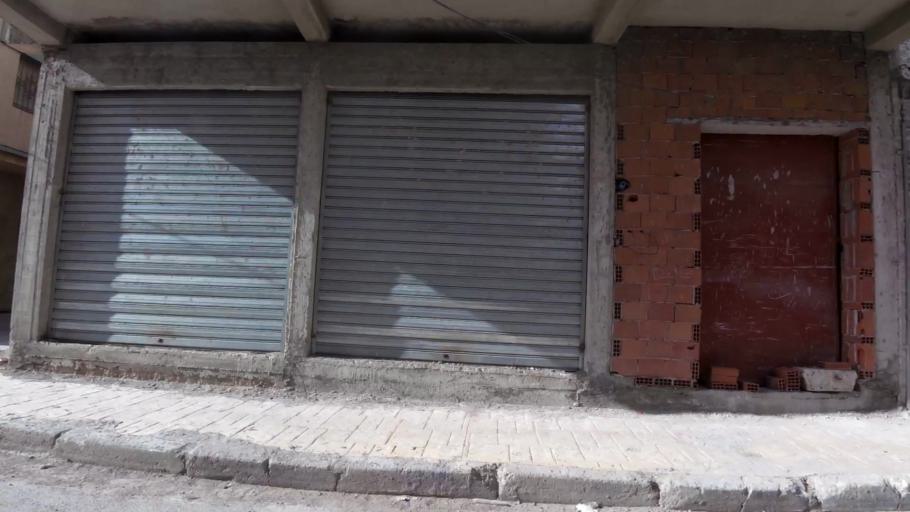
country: MA
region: Tanger-Tetouan
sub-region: Tetouan
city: Martil
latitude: 35.6123
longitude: -5.2817
